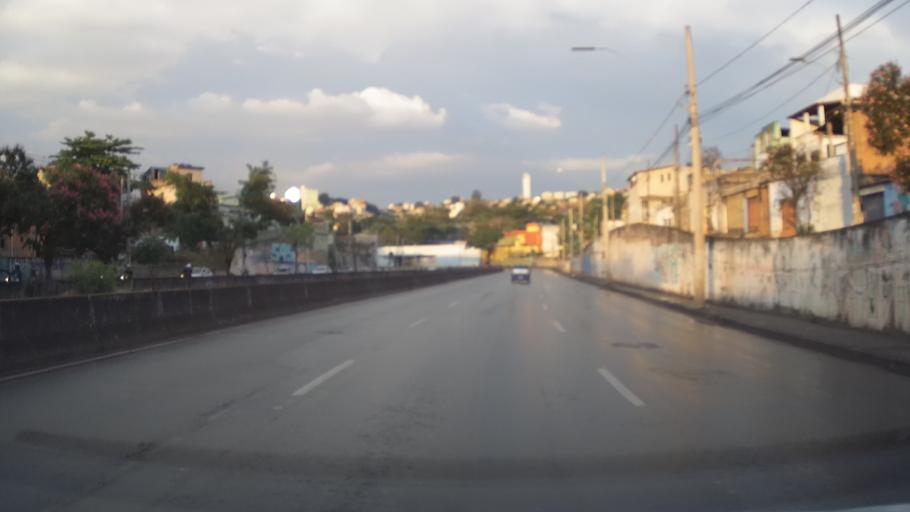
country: BR
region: Minas Gerais
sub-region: Belo Horizonte
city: Belo Horizonte
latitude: -19.9530
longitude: -43.9849
